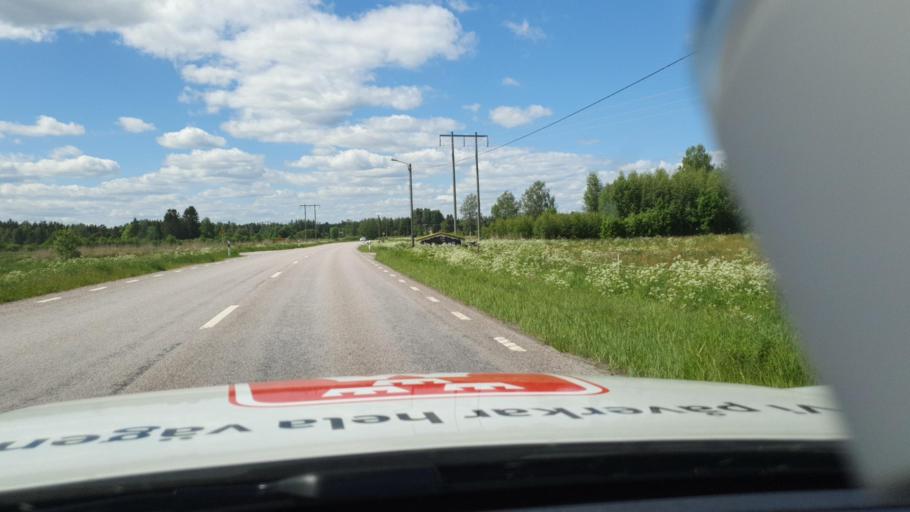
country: SE
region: Uppsala
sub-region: Tierps Kommun
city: Karlholmsbruk
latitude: 60.5023
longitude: 17.6684
